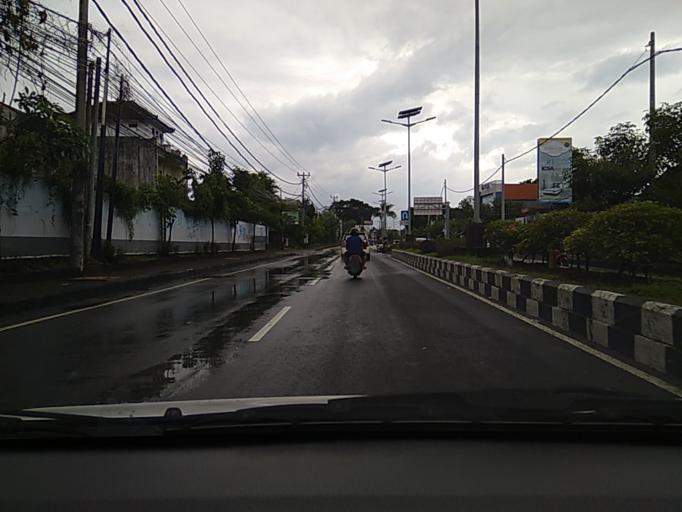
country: ID
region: Bali
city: Bualu
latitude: -8.7895
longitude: 115.2107
